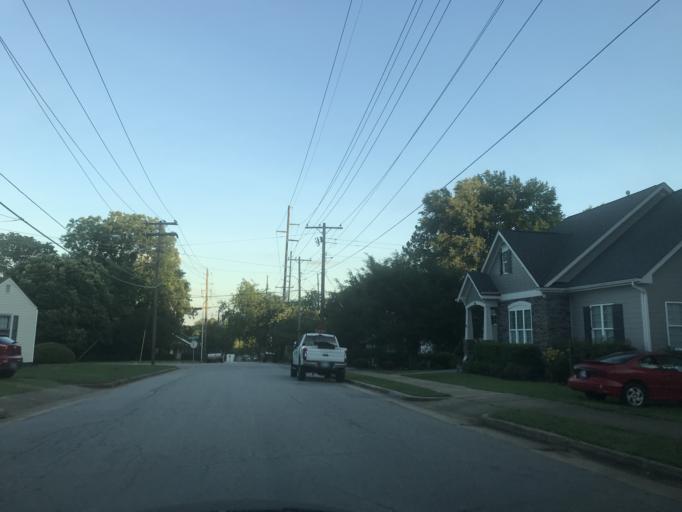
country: US
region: North Carolina
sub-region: Wake County
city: Raleigh
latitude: 35.8056
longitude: -78.6316
